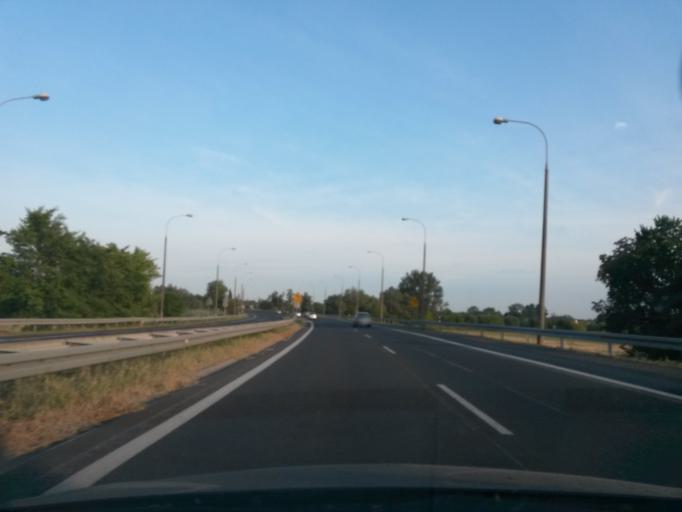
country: PL
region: Masovian Voivodeship
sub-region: Powiat nowodworski
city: Zakroczym
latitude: 52.4227
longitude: 20.6595
